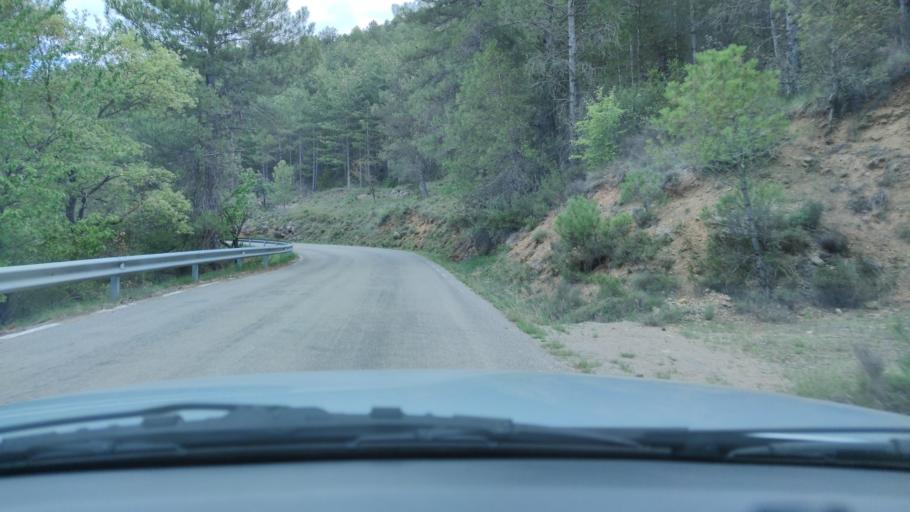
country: ES
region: Catalonia
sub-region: Provincia de Lleida
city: Coll de Nargo
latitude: 42.2441
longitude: 1.3510
